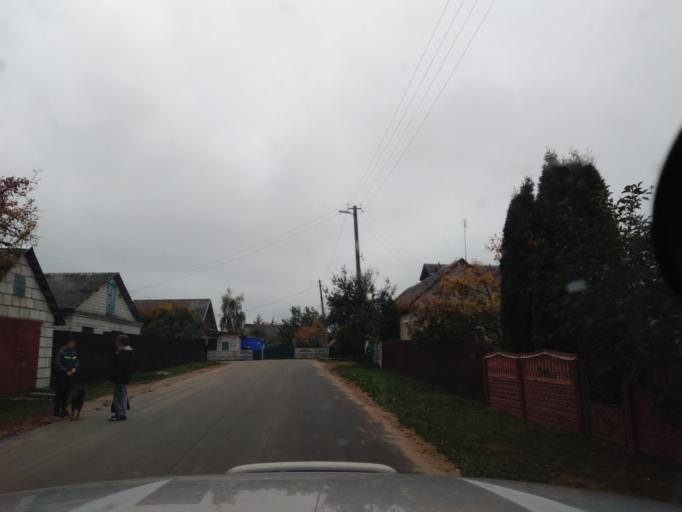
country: BY
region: Minsk
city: Kapyl'
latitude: 53.1417
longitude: 27.0918
